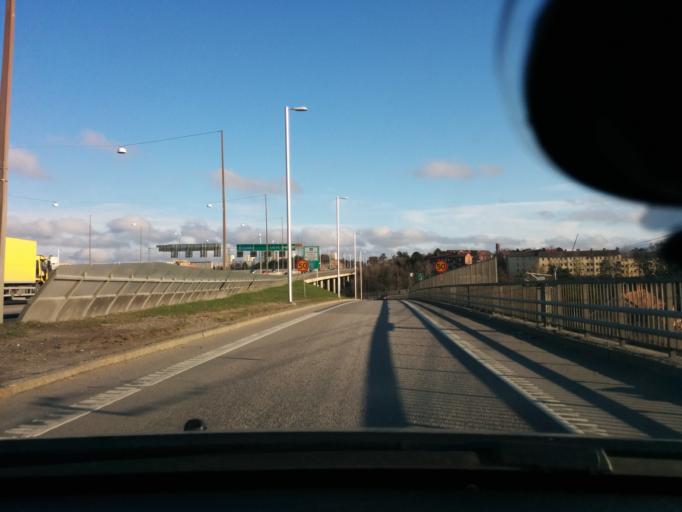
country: SE
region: Stockholm
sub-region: Solna Kommun
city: Solna
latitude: 59.3170
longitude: 18.0002
